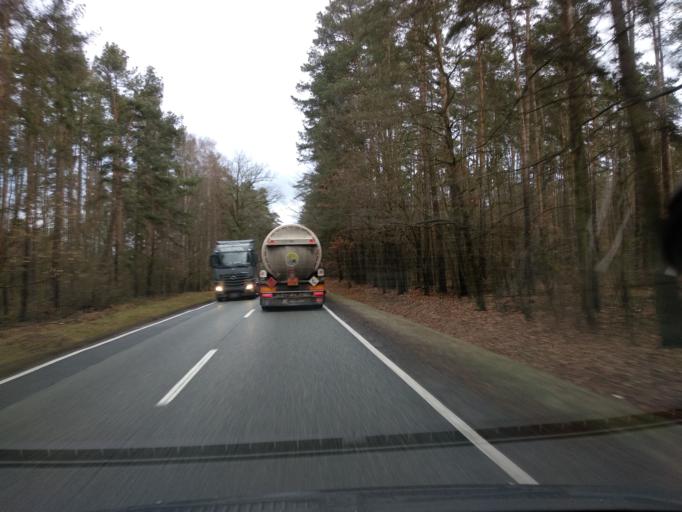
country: PL
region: Lower Silesian Voivodeship
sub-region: Powiat olesnicki
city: Twardogora
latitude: 51.3028
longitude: 17.5378
